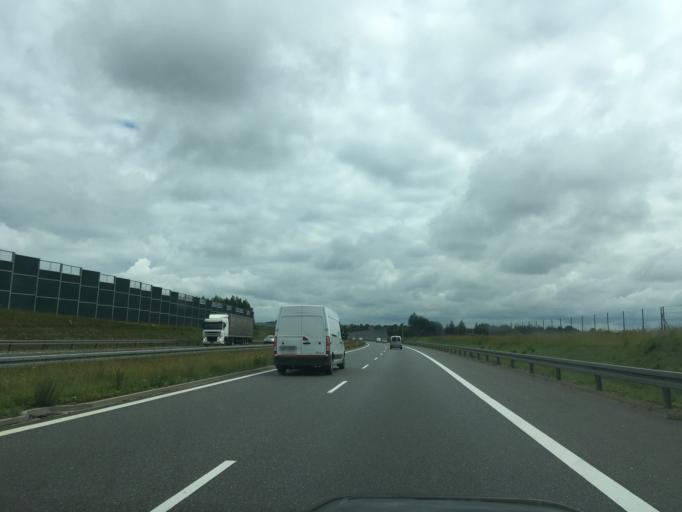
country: PL
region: Lublin Voivodeship
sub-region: Powiat lubelski
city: Jakubowice Murowane
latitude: 51.2921
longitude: 22.6109
